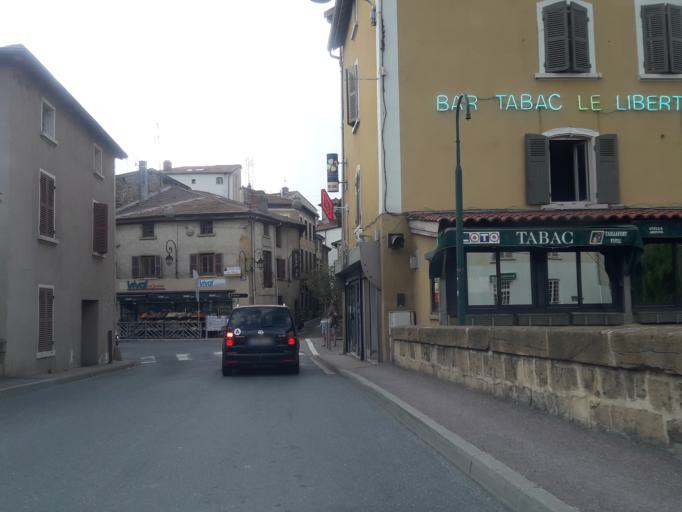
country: FR
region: Rhone-Alpes
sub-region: Departement du Rhone
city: Saint-Germain-Nuelles
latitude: 45.8351
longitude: 4.6184
